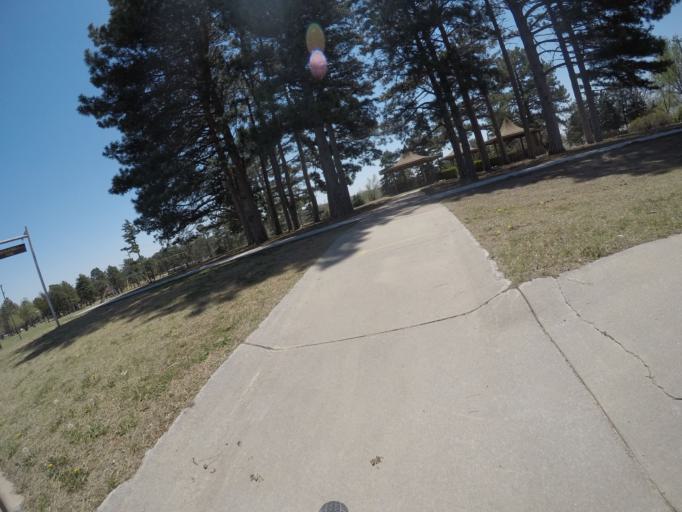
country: US
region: Kansas
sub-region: Pratt County
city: Pratt
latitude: 37.6407
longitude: -98.7344
